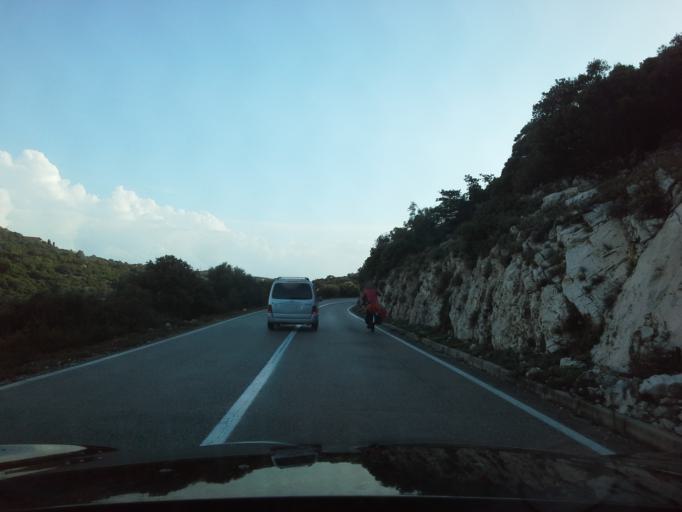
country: HR
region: Primorsko-Goranska
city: Mali Losinj
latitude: 44.5960
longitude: 14.4085
